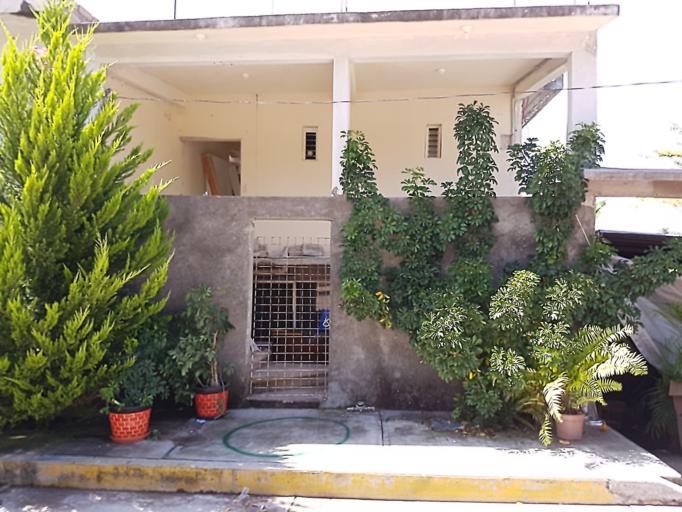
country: MX
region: Oaxaca
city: Ciudad de Huajuapam de Leon
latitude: 17.8045
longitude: -97.7960
